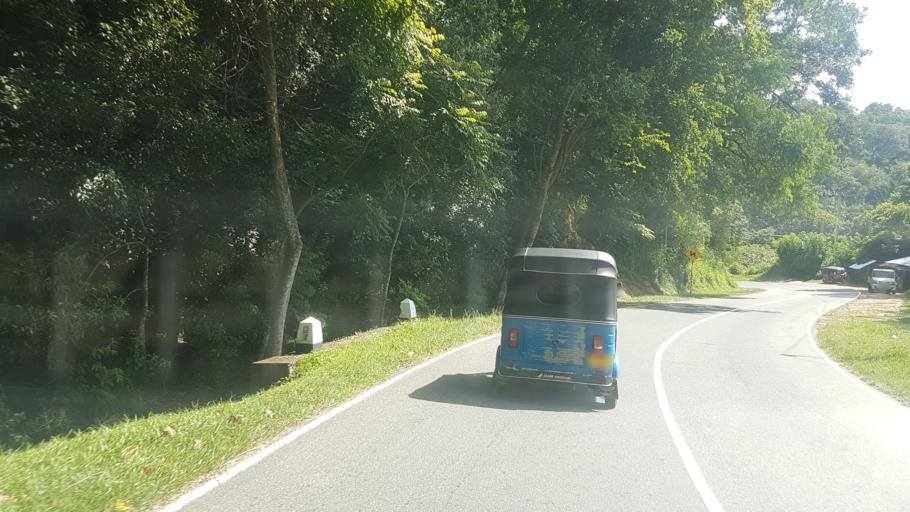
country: LK
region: Uva
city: Haputale
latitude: 6.8034
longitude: 81.0902
